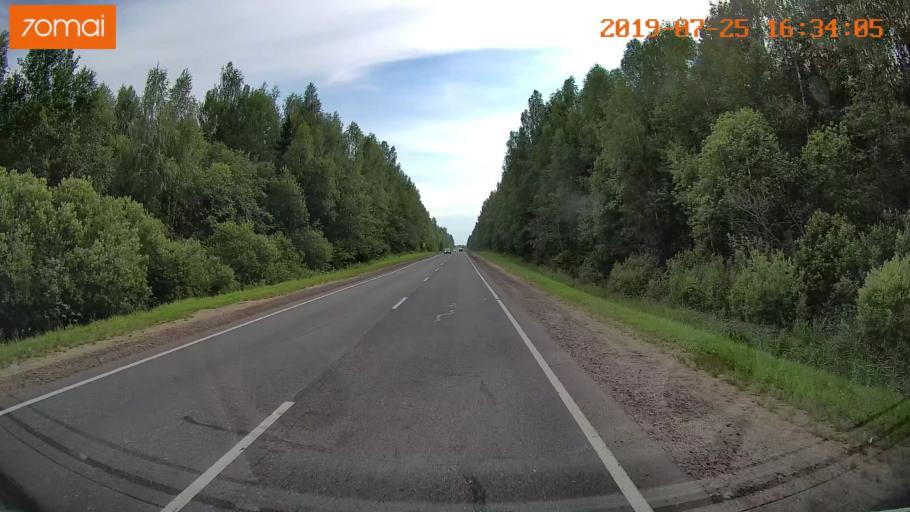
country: RU
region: Ivanovo
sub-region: Privolzhskiy Rayon
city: Ples
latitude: 57.4205
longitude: 41.4441
